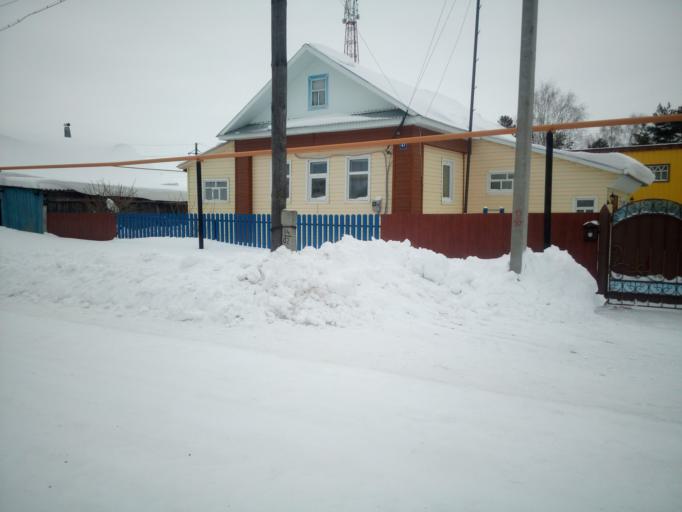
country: RU
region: Bashkortostan
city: Kaltasy
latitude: 55.8058
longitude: 54.5332
